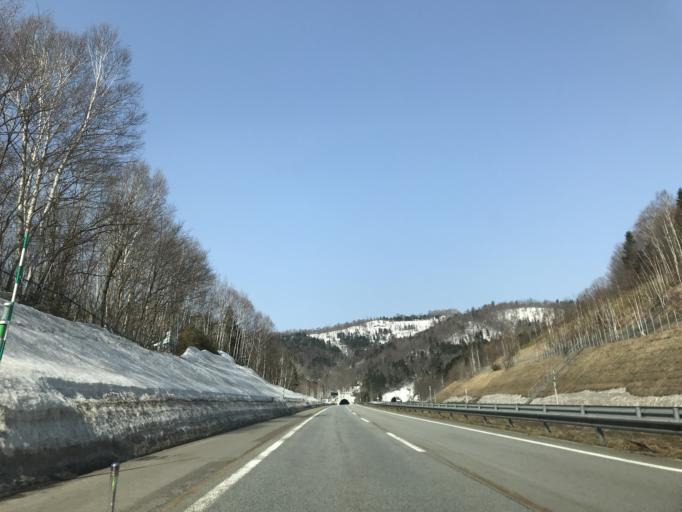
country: JP
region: Hokkaido
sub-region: Asahikawa-shi
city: Asahikawa
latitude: 43.7921
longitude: 142.2723
